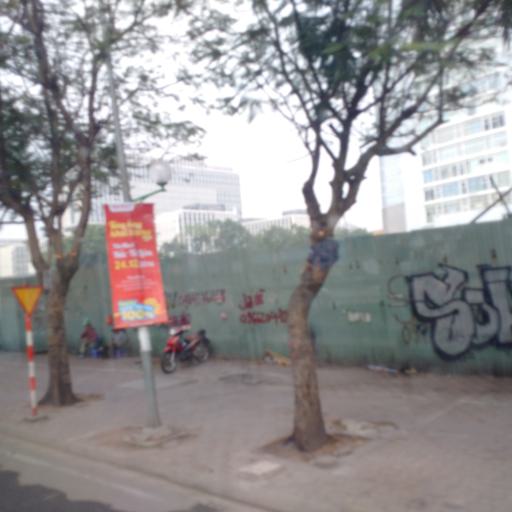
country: VN
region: Ha Noi
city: Cau Dien
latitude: 21.0461
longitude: 105.7828
